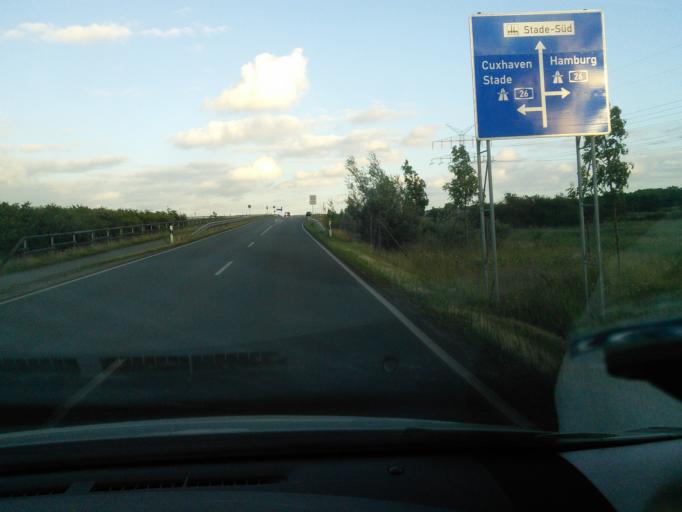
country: DE
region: Lower Saxony
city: Agathenburg
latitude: 53.5820
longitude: 9.5164
